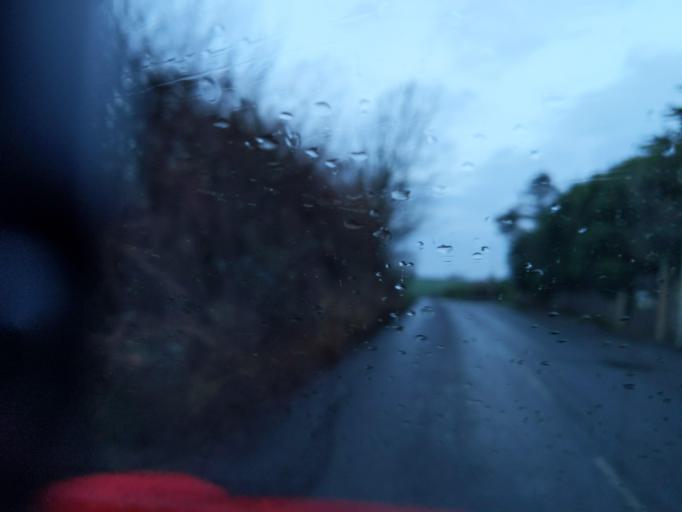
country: GB
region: England
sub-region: Devon
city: Wembury
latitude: 50.3390
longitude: -4.0736
